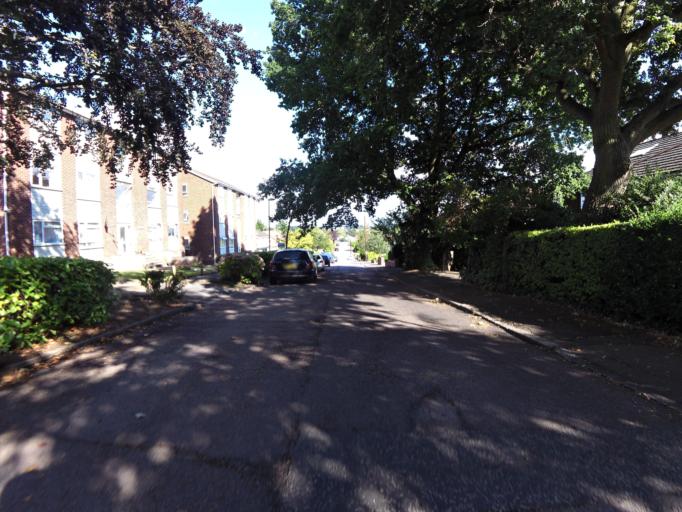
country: GB
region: England
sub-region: Greater London
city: Barnet
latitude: 51.6445
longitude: -0.1776
